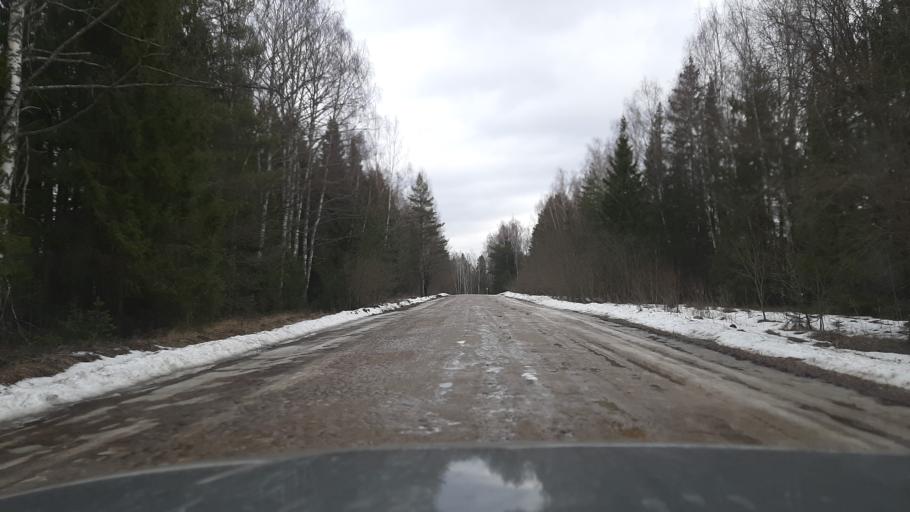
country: RU
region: Ivanovo
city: Teykovo
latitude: 56.8899
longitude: 40.6586
